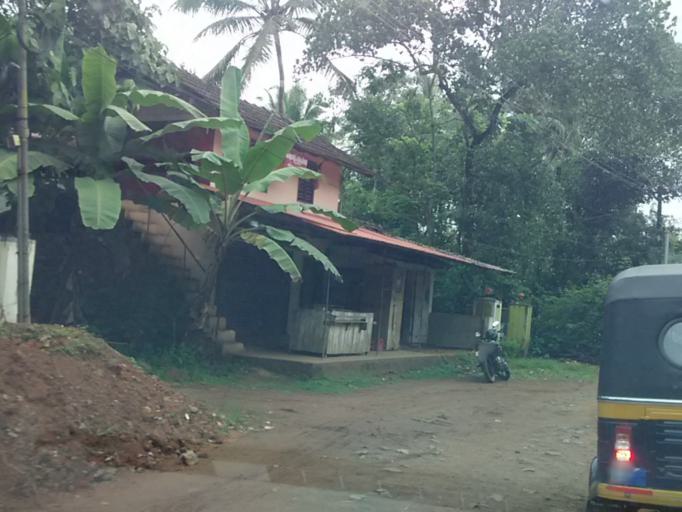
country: IN
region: Kerala
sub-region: Kozhikode
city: Kunnamangalam
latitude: 11.3061
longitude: 75.8933
